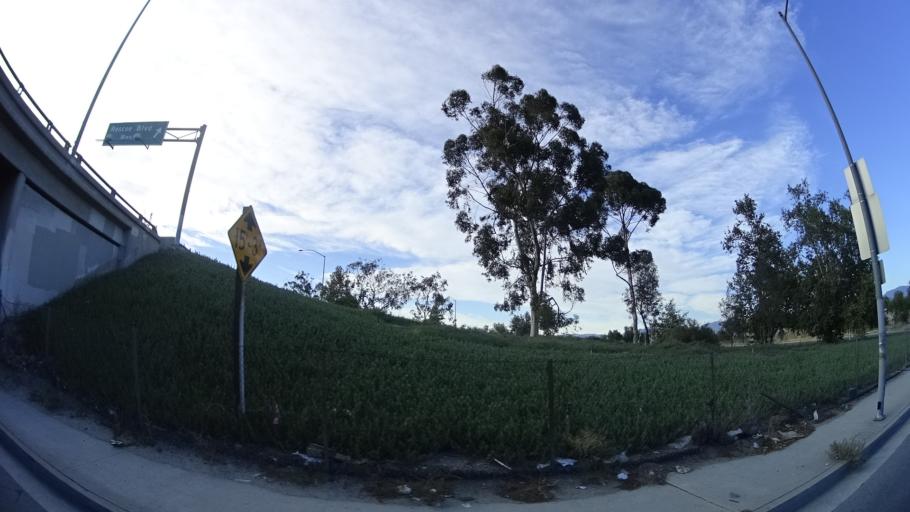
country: US
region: California
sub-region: Los Angeles County
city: Van Nuys
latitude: 34.2218
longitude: -118.4096
